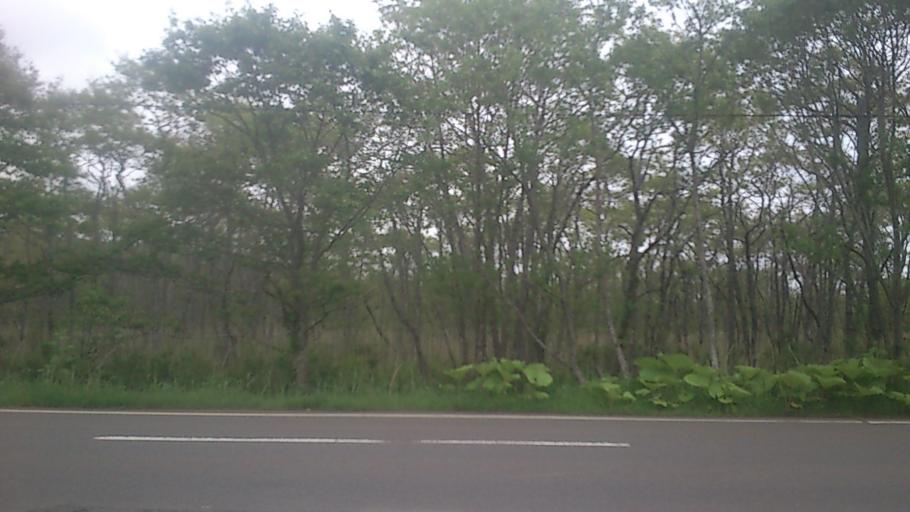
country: JP
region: Hokkaido
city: Nemuro
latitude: 43.0872
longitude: 145.0609
